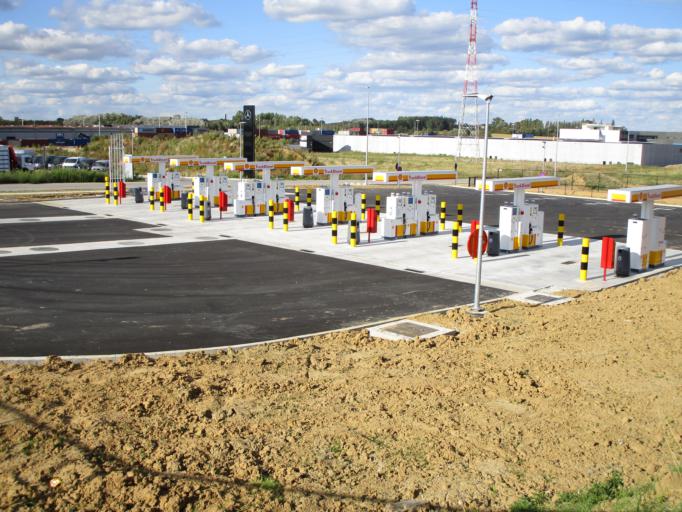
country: BE
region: Wallonia
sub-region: Province du Hainaut
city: Mouscron
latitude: 50.7710
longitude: 3.1987
